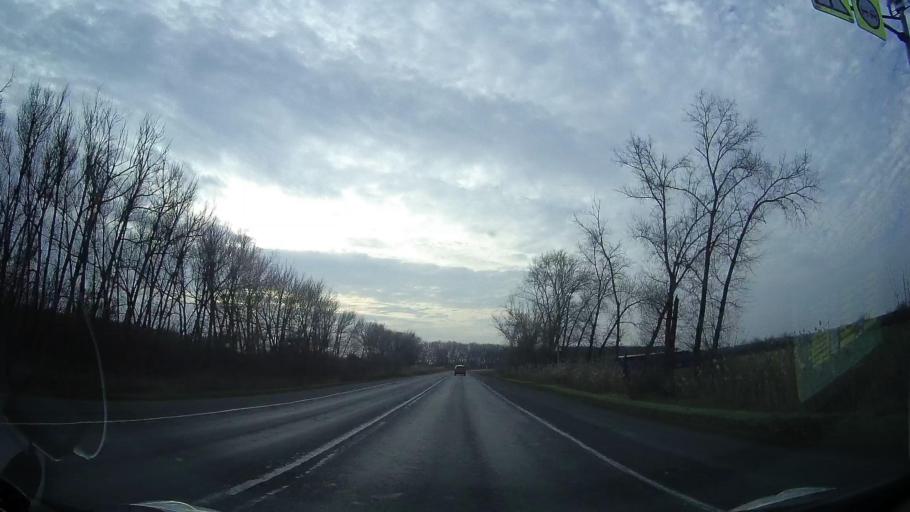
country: RU
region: Rostov
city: Starocherkasskaya
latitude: 47.1554
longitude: 40.2060
